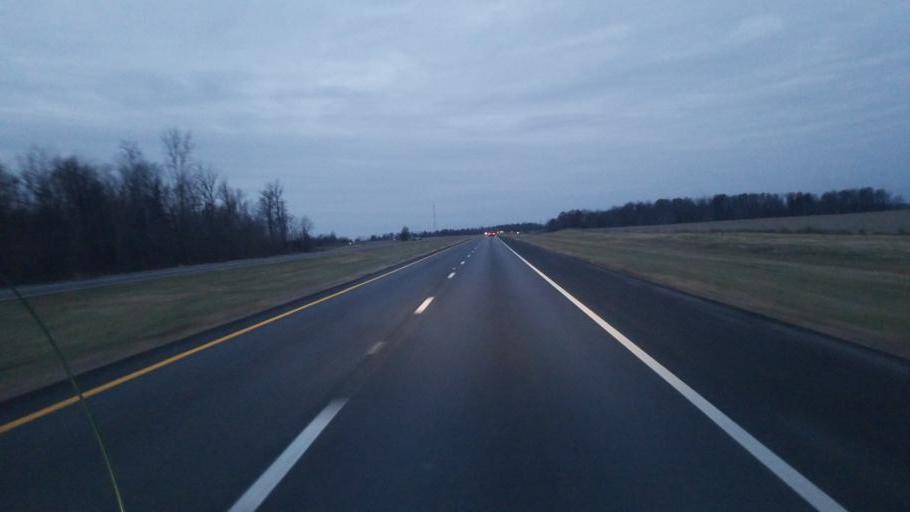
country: US
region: Ohio
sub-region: Hardin County
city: Forest
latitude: 40.8250
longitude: -83.4570
